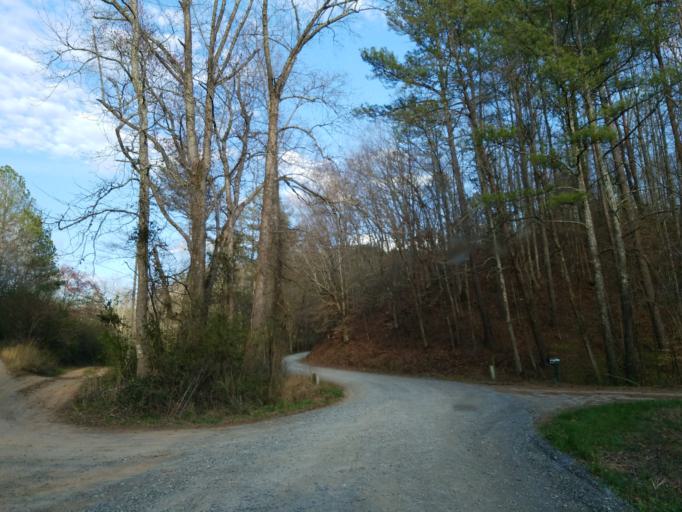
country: US
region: Georgia
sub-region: Bartow County
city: Rydal
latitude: 34.5028
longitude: -84.6366
